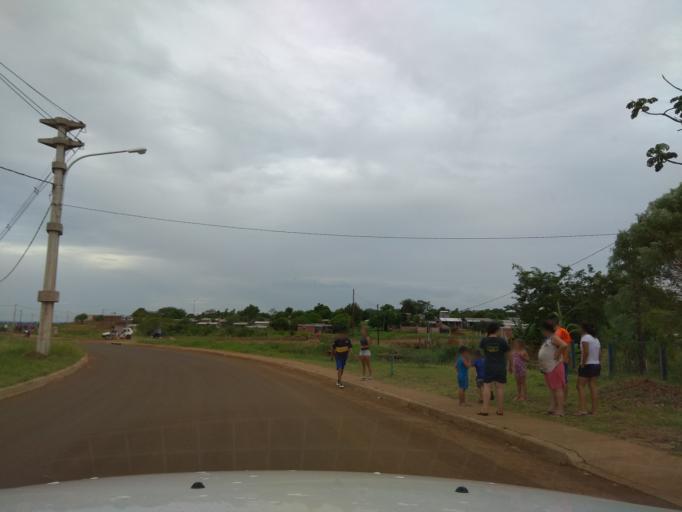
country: AR
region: Misiones
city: Garupa
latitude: -27.4354
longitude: -55.8631
